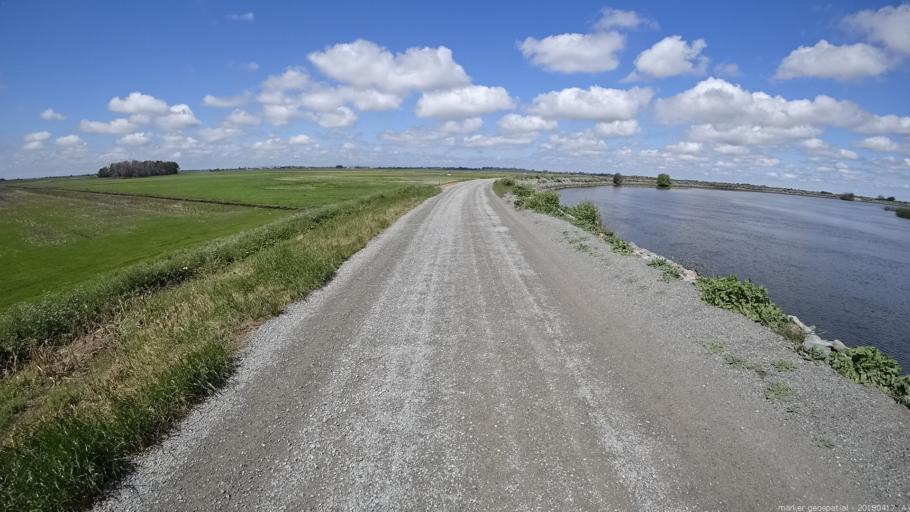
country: US
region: California
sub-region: Sacramento County
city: Walnut Grove
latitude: 38.1408
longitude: -121.5603
